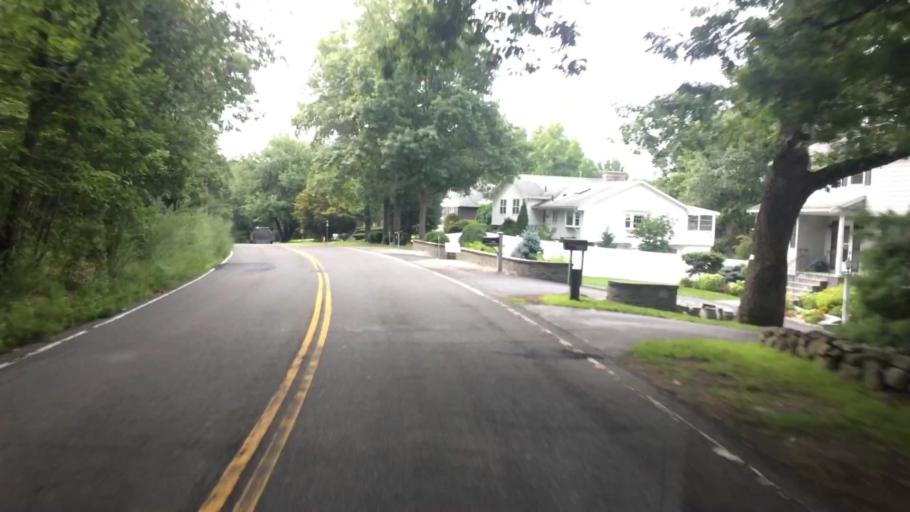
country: US
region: Massachusetts
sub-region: Middlesex County
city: Winchester
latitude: 42.4419
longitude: -71.1238
